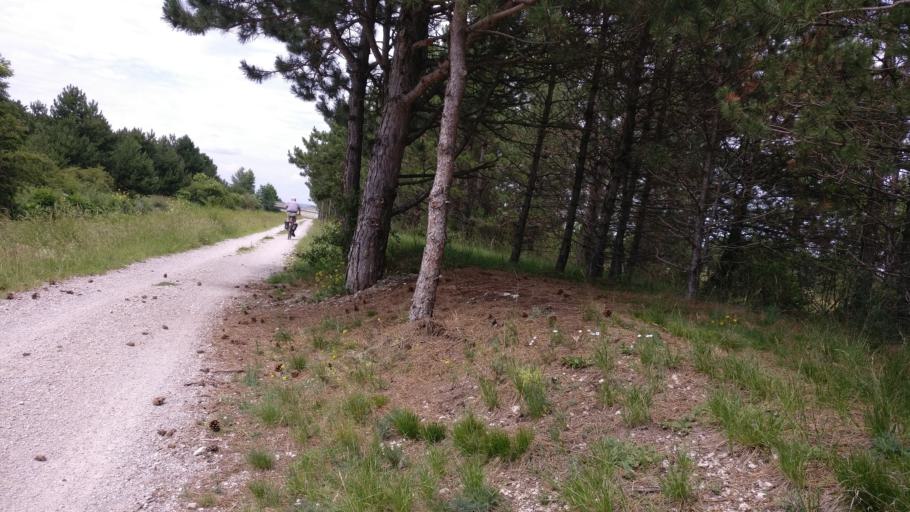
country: AT
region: Lower Austria
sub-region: Politischer Bezirk Wiener Neustadt
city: Sollenau
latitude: 47.8922
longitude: 16.2782
